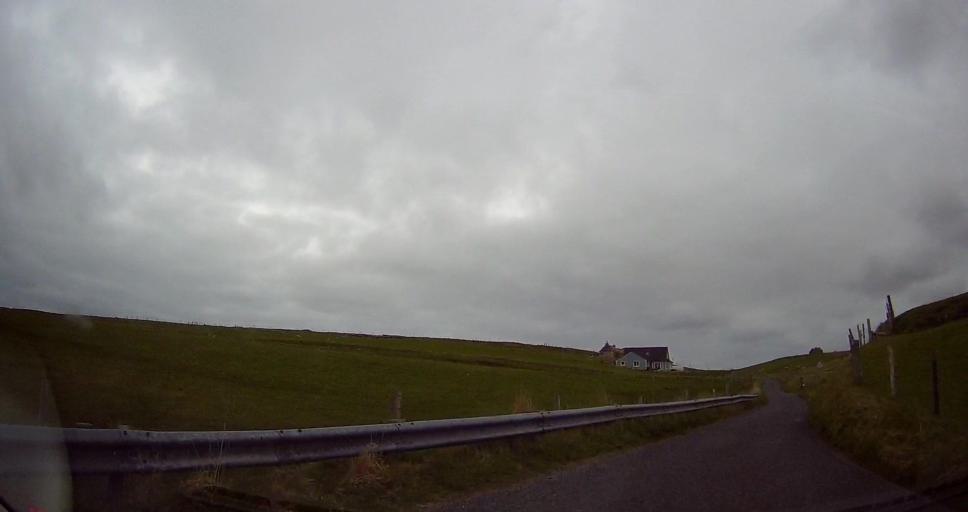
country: GB
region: Scotland
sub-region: Shetland Islands
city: Shetland
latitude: 60.8022
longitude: -0.8775
